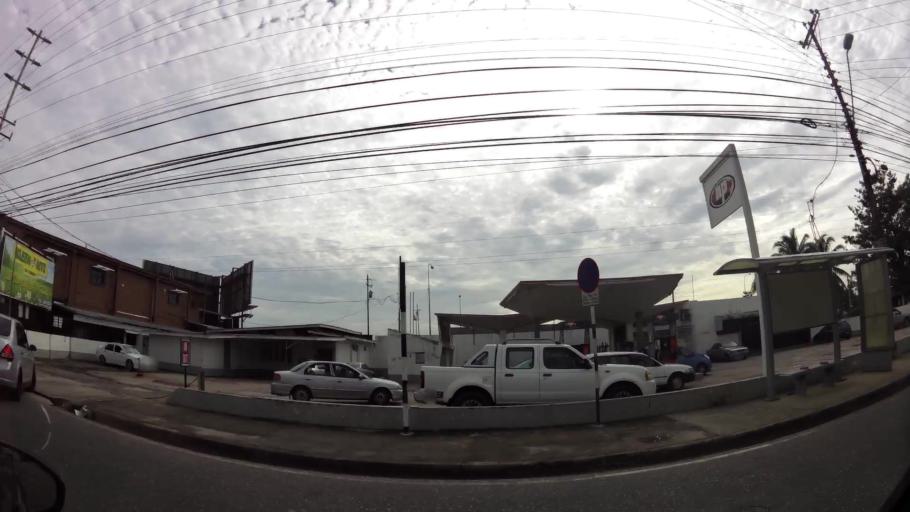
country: TT
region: City of Port of Spain
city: Mucurapo
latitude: 10.6728
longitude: -61.5400
